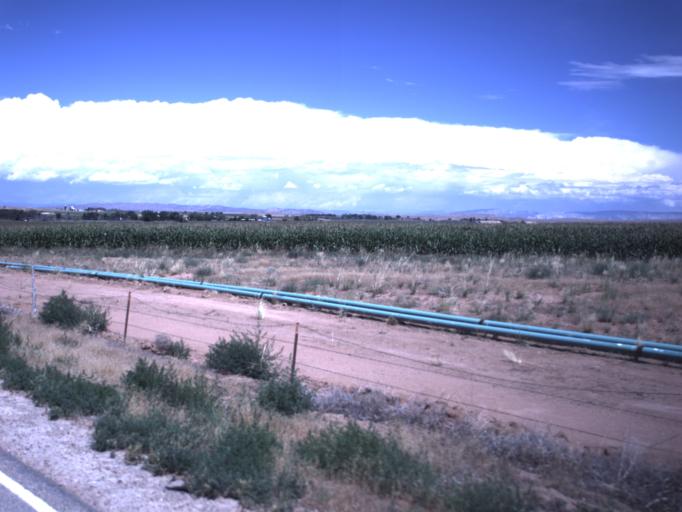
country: US
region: Utah
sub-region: Uintah County
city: Naples
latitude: 40.1752
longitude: -109.6645
